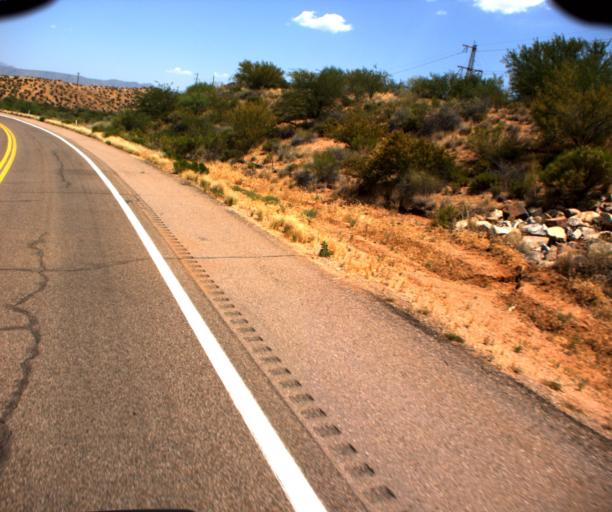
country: US
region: Arizona
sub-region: Gila County
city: Tonto Basin
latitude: 33.6366
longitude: -111.0761
